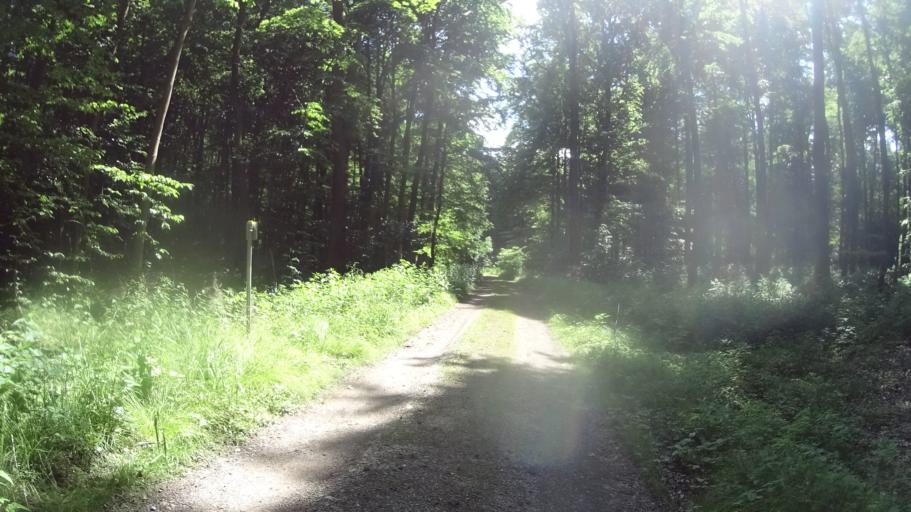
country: DE
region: Lower Saxony
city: Elbe
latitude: 52.0786
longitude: 10.3406
